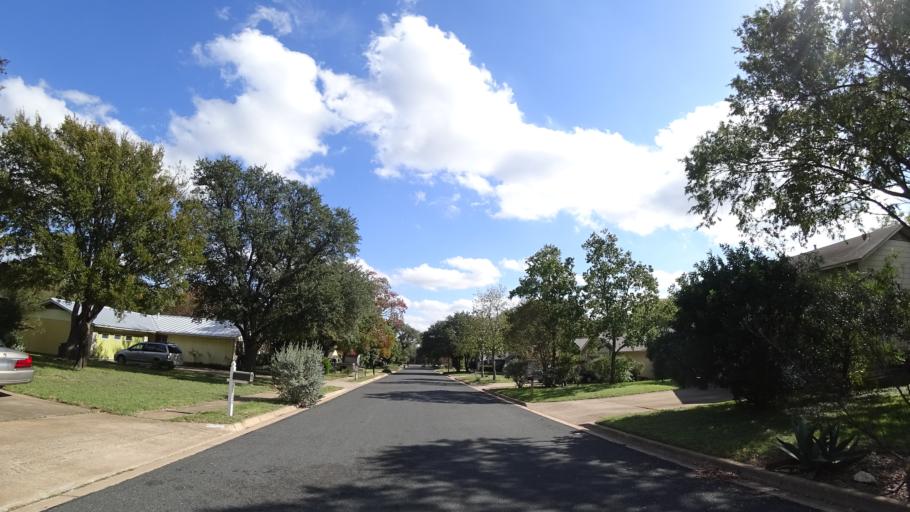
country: US
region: Texas
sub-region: Travis County
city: Wells Branch
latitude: 30.4161
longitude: -97.7216
